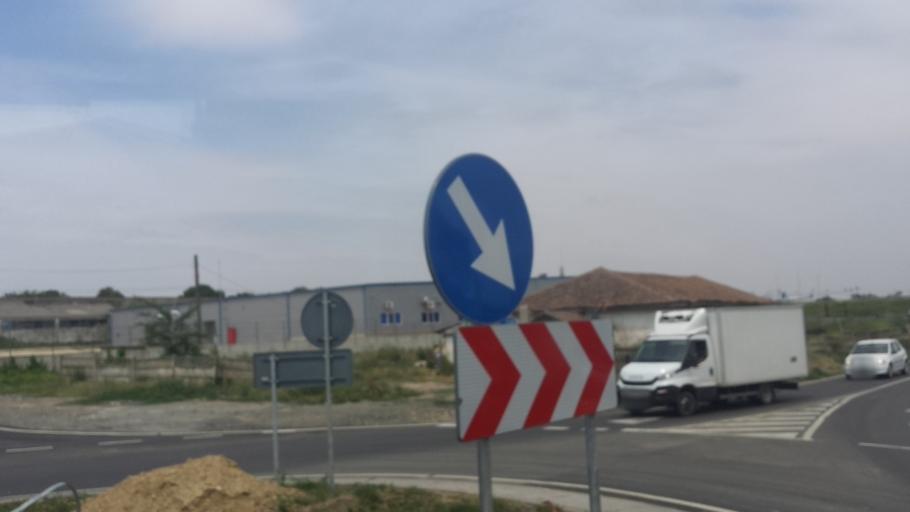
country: RO
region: Constanta
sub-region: Comuna Ovidiu
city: Ovidiu
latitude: 44.2601
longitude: 28.5541
